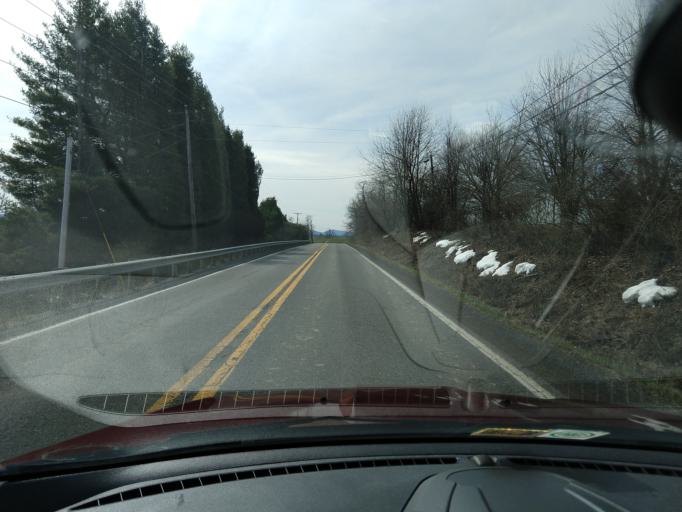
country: US
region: West Virginia
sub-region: Greenbrier County
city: Lewisburg
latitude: 37.9128
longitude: -80.3842
